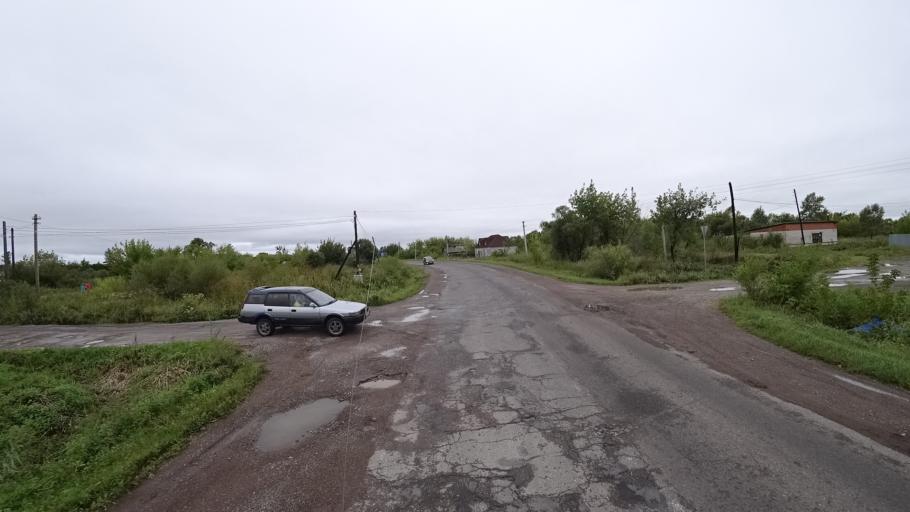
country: RU
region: Primorskiy
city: Monastyrishche
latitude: 44.2042
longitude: 132.4714
